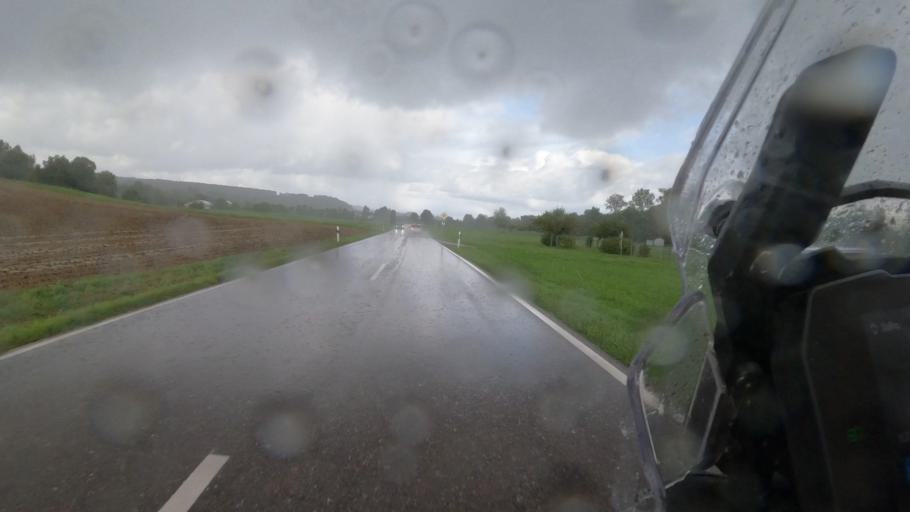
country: DE
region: Baden-Wuerttemberg
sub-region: Freiburg Region
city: Jestetten
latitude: 47.6429
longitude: 8.5574
